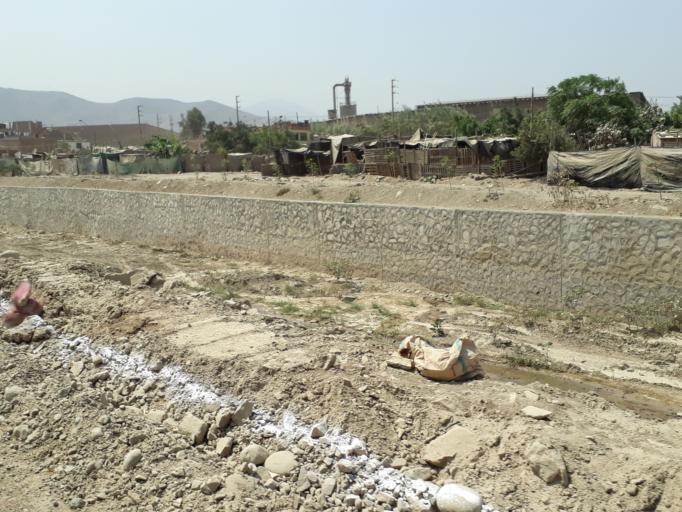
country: PE
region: Lima
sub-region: Lima
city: Santa Maria
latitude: -11.9956
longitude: -76.9122
